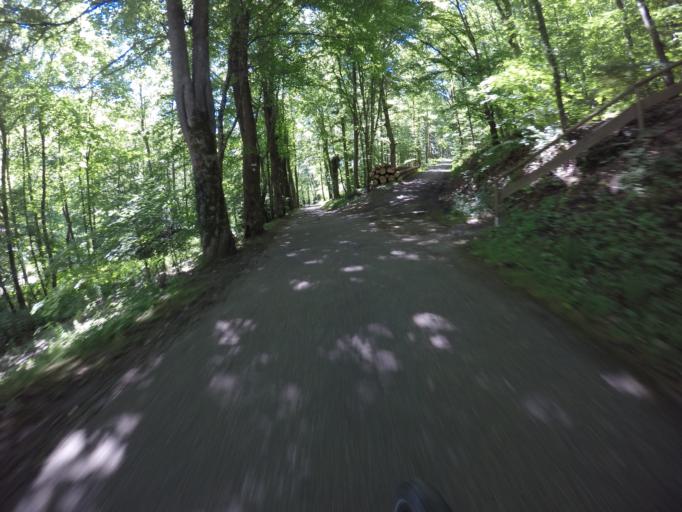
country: DE
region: Baden-Wuerttemberg
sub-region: Karlsruhe Region
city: Pforzheim
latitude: 48.8735
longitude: 8.7082
